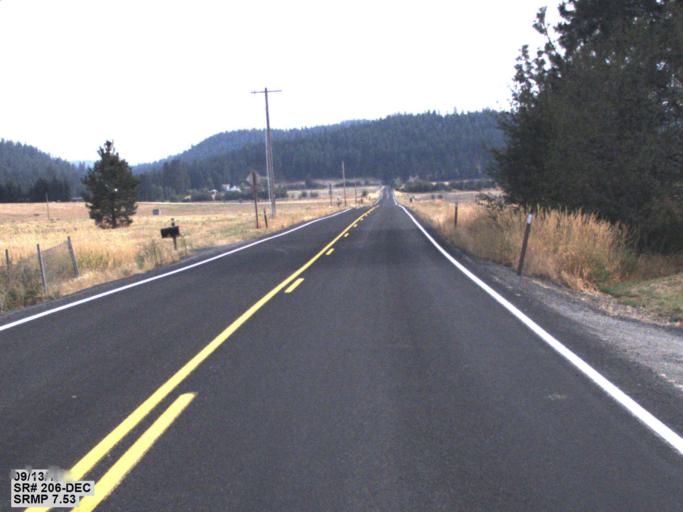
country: US
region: Washington
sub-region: Spokane County
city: Trentwood
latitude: 47.8114
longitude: -117.2129
